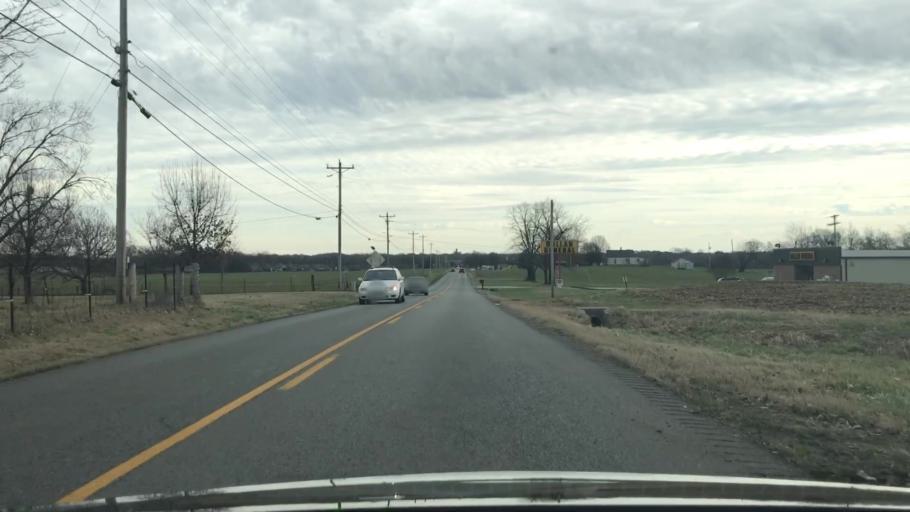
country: US
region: Kentucky
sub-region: Christian County
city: Hopkinsville
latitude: 36.8624
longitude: -87.5362
